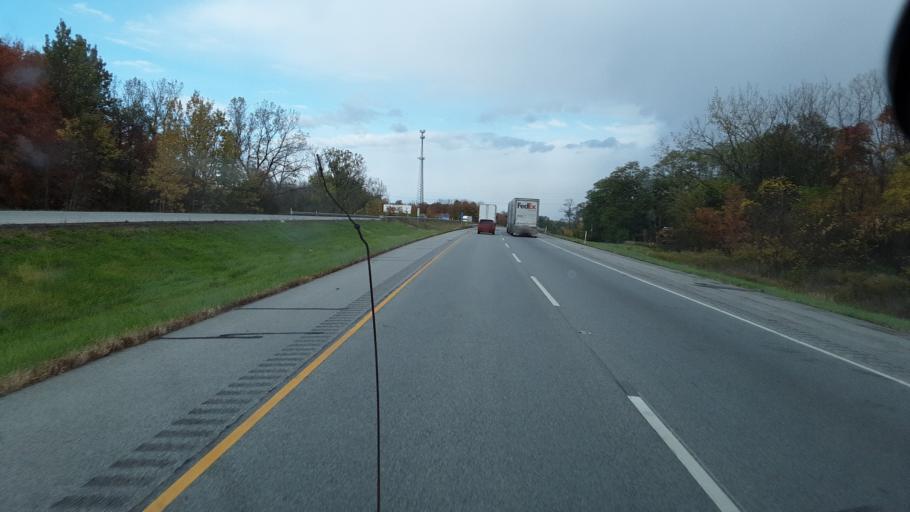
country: US
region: Indiana
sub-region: LaPorte County
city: LaPorte
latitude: 41.6530
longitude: -86.7661
